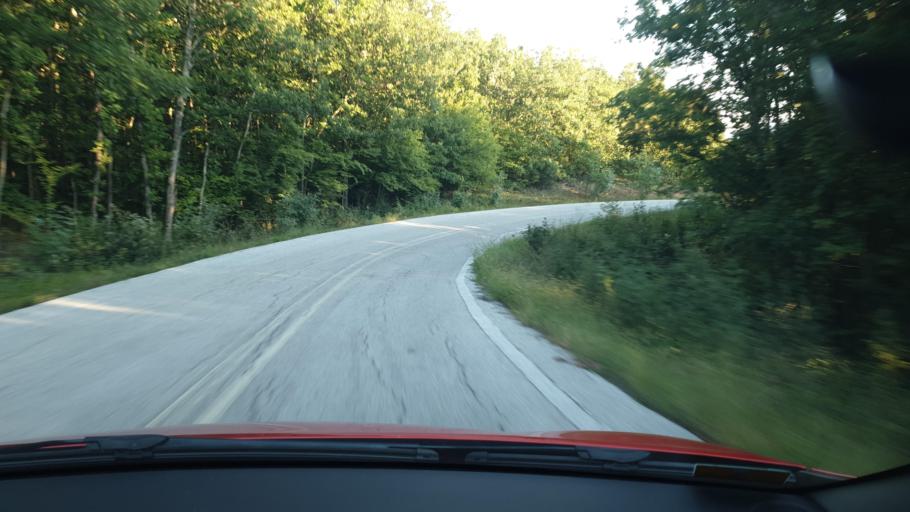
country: GR
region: Central Macedonia
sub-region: Nomos Chalkidikis
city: Galatista
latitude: 40.5359
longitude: 23.2769
